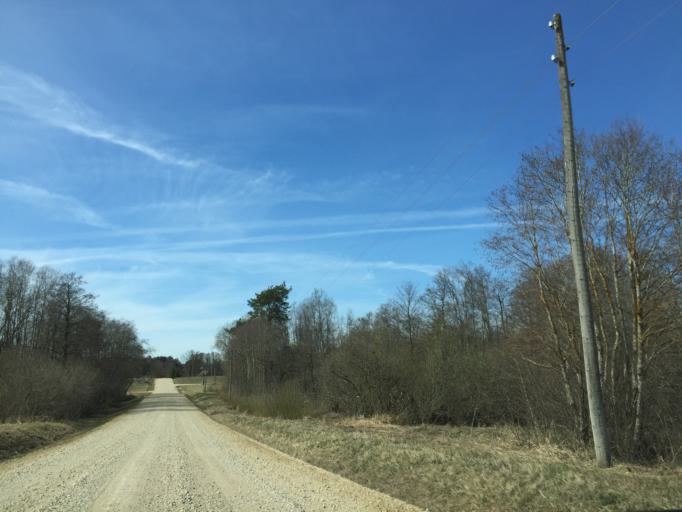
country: EE
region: Vorumaa
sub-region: Antsla vald
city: Vana-Antsla
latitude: 57.9550
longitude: 26.3603
